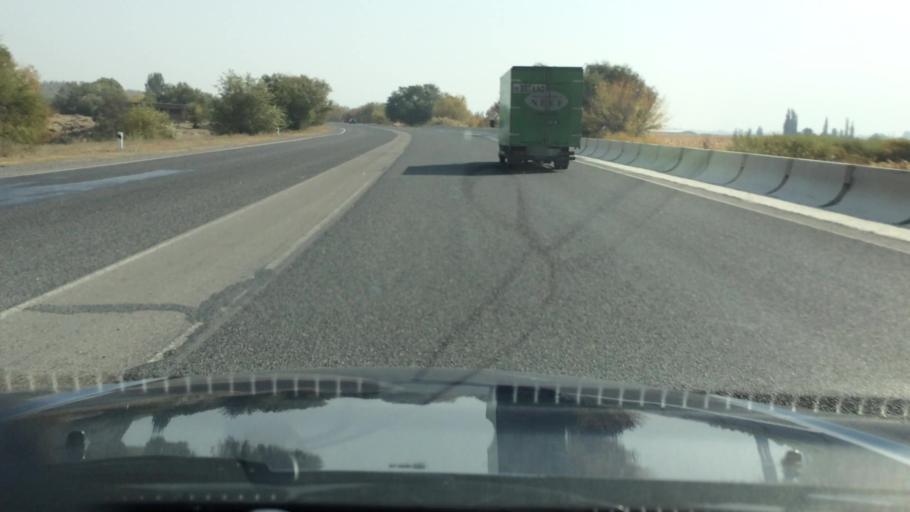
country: KG
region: Chuy
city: Ivanovka
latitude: 42.9407
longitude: 74.9693
